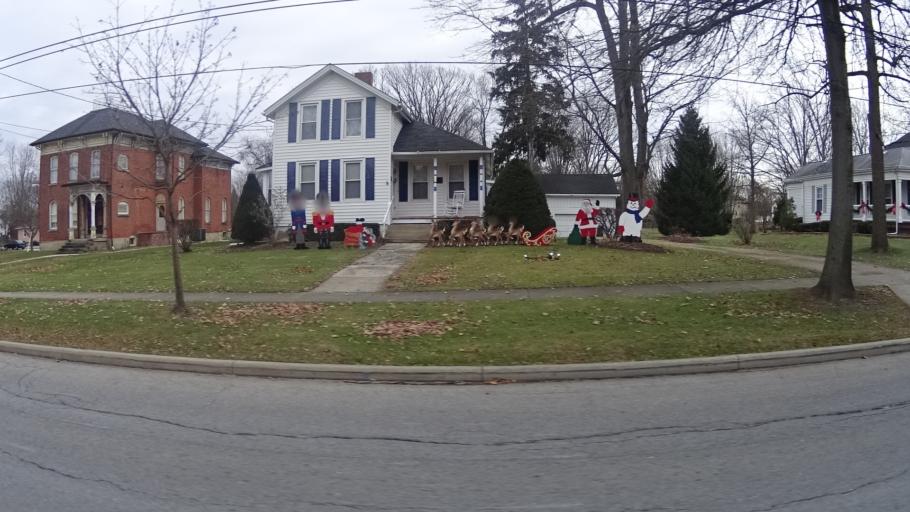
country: US
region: Ohio
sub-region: Lorain County
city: Wellington
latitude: 41.1631
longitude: -82.2177
